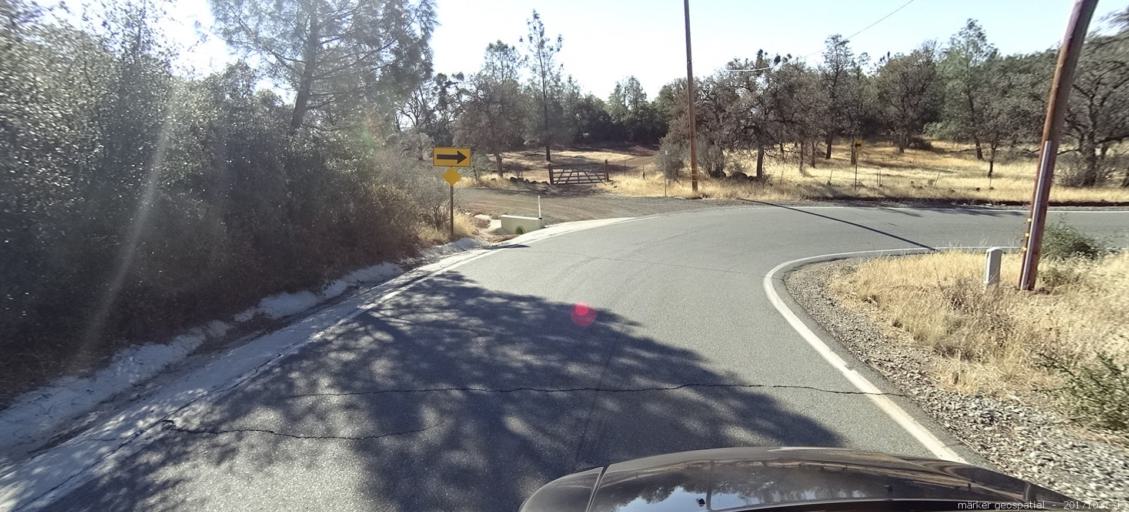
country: US
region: California
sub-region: Shasta County
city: Shingletown
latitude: 40.4650
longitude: -121.8821
